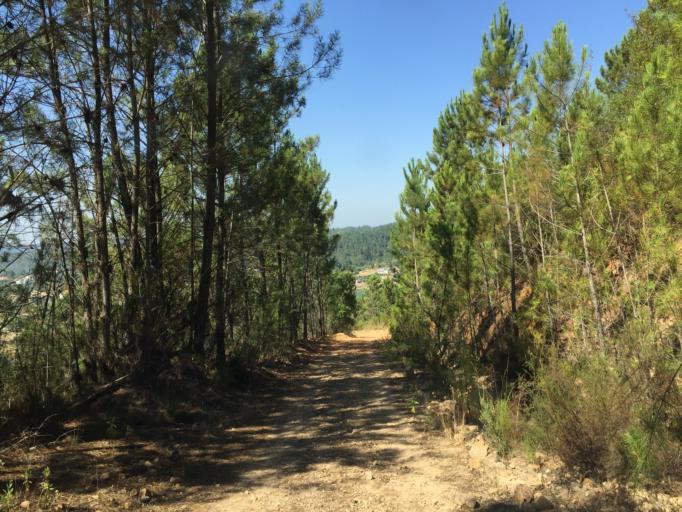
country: PT
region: Santarem
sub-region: Ferreira do Zezere
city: Ferreira do Zezere
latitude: 39.6529
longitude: -8.2382
